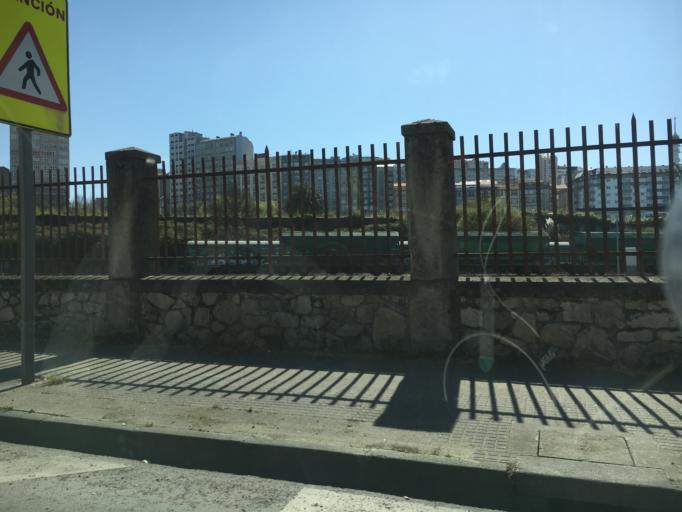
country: ES
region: Galicia
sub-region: Provincia da Coruna
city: A Coruna
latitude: 43.3557
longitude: -8.3920
